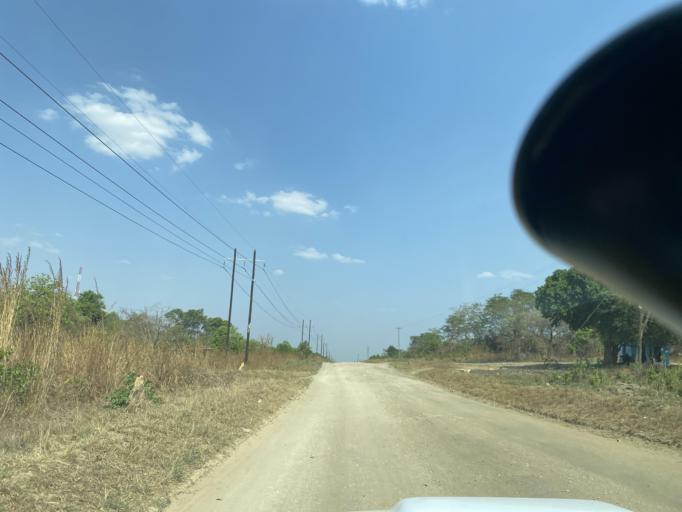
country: ZM
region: Lusaka
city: Lusaka
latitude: -15.3098
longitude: 28.0468
